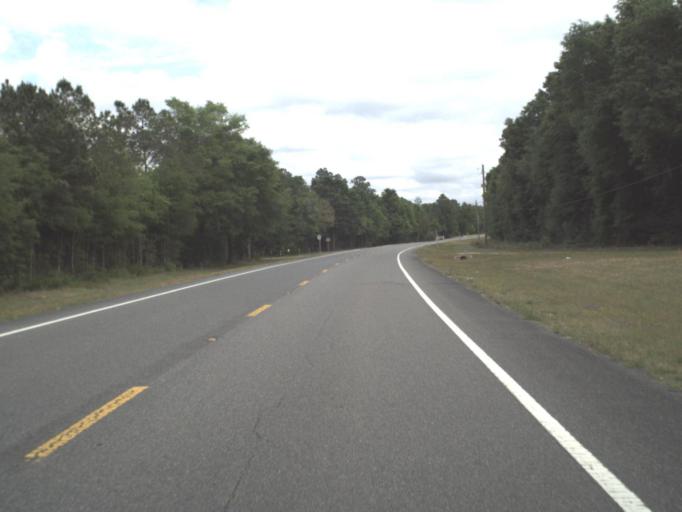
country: US
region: Florida
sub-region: Santa Rosa County
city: Point Baker
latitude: 30.6979
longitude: -87.0659
